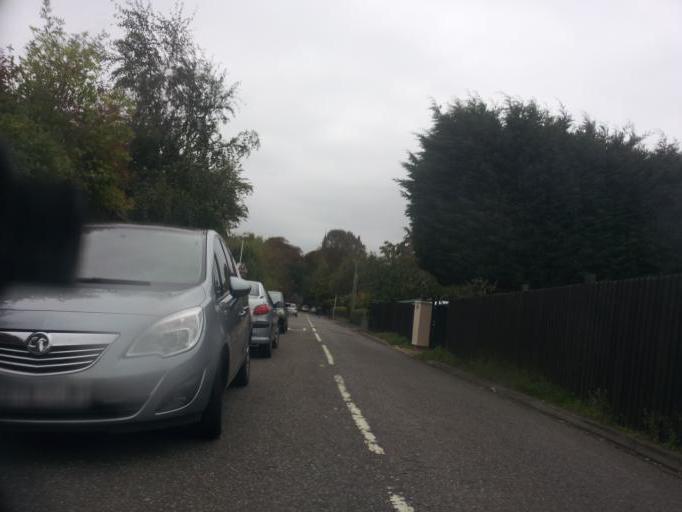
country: GB
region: England
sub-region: Kent
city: Sittingbourne
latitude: 51.3346
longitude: 0.7668
